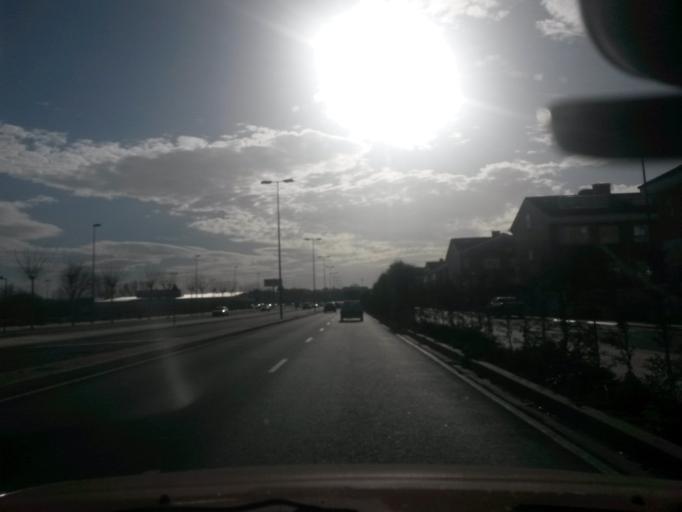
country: ES
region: Castille and Leon
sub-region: Provincia de Salamanca
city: Santa Marta de Tormes
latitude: 40.9560
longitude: -5.6433
